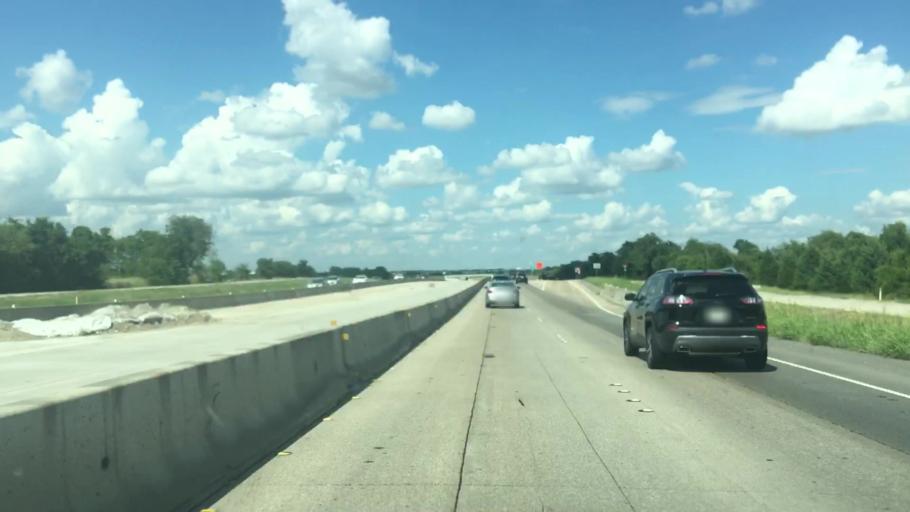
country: US
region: Texas
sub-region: Ellis County
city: Red Oak
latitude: 32.4886
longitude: -96.8278
